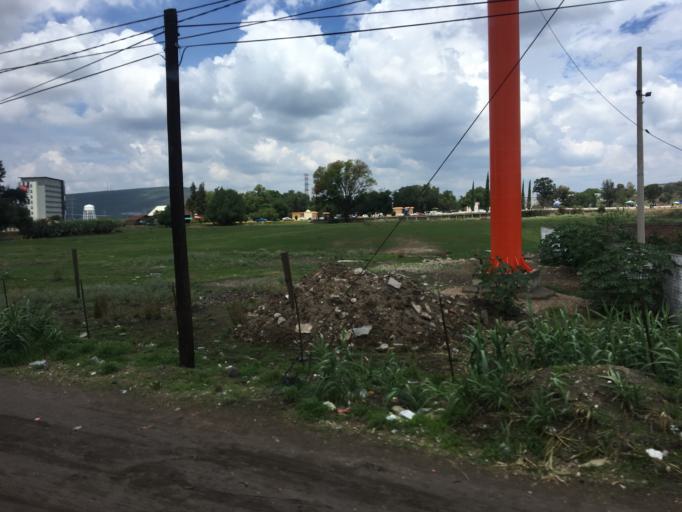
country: MX
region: Guanajuato
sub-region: Irapuato
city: Ex-Hacienda del Copal
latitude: 20.7238
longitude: -101.3457
